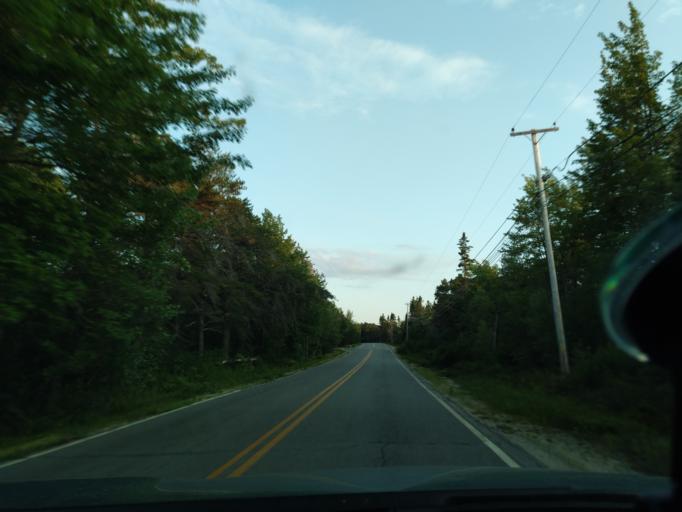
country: US
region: Maine
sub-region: Hancock County
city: Gouldsboro
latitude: 44.3803
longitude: -68.0364
